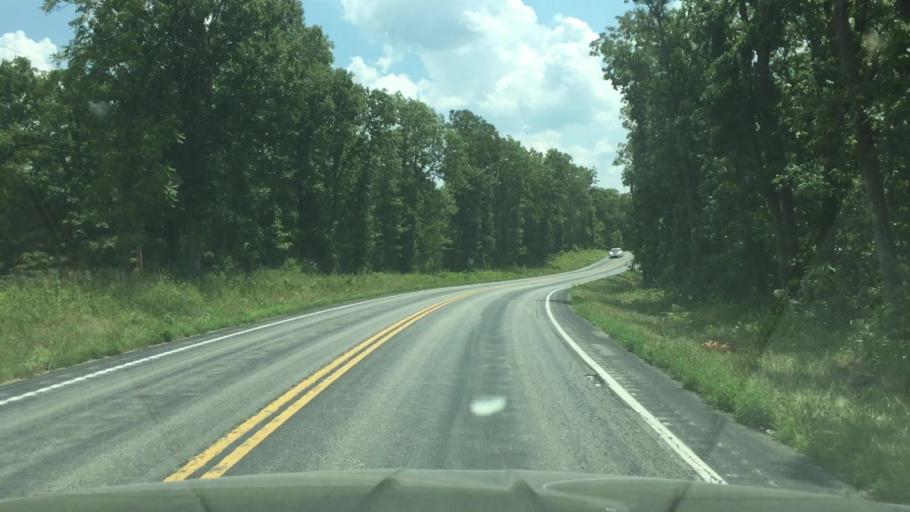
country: US
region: Missouri
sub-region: Camden County
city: Osage Beach
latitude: 38.1351
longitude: -92.5688
